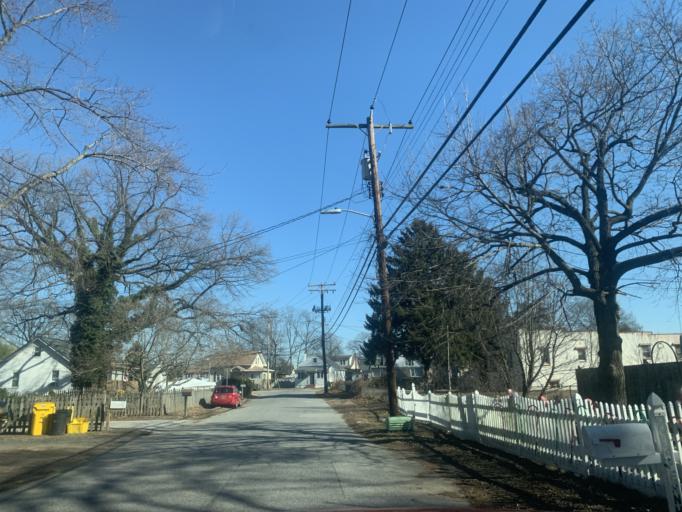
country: US
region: Maryland
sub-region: Anne Arundel County
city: Riviera Beach
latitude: 39.1692
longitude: -76.5279
